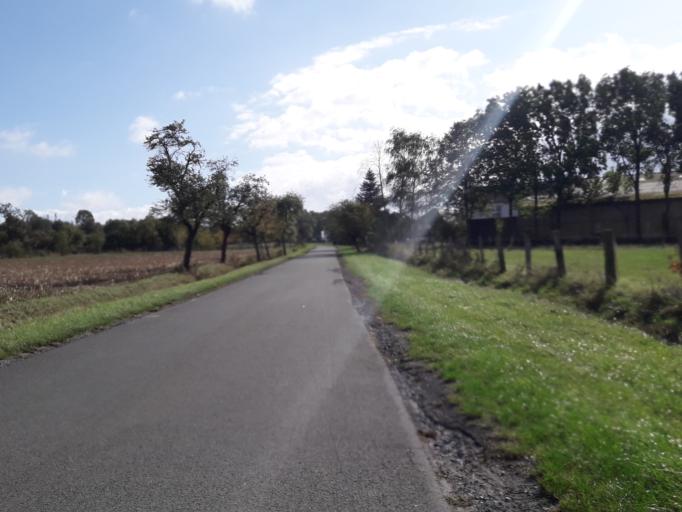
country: DE
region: North Rhine-Westphalia
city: Bad Lippspringe
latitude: 51.7411
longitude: 8.8058
